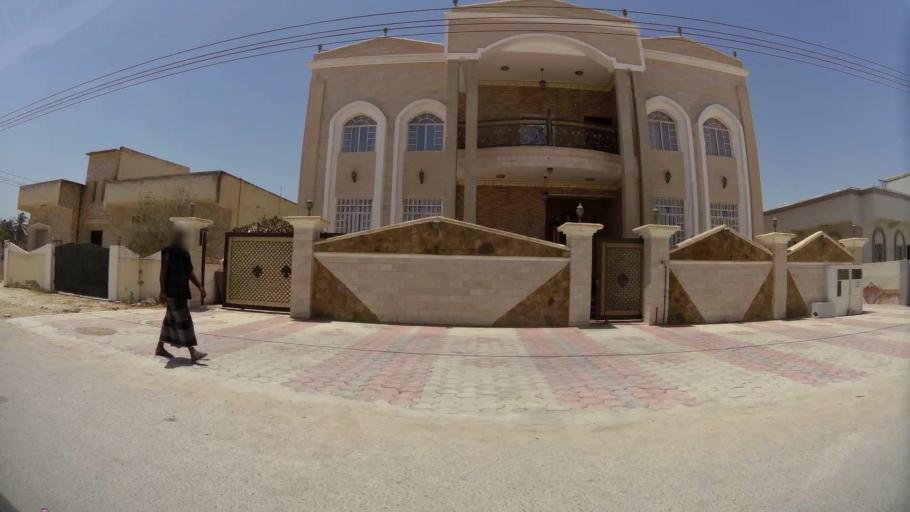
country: OM
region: Zufar
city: Salalah
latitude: 17.0857
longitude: 54.1515
